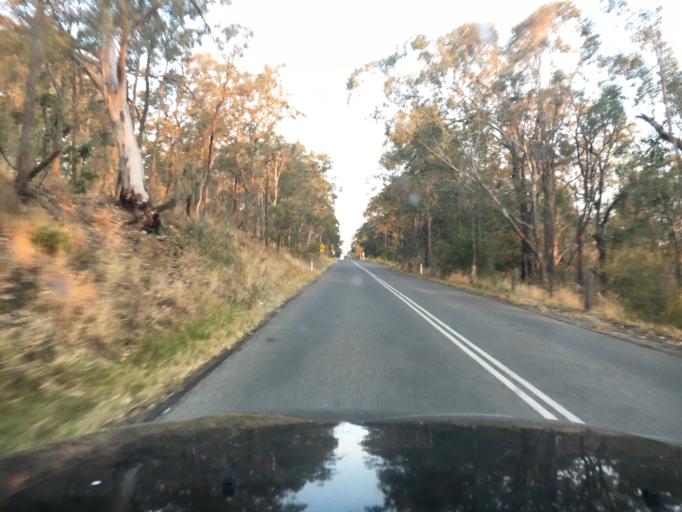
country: AU
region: New South Wales
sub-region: Cessnock
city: Branxton
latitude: -32.6153
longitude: 151.3535
